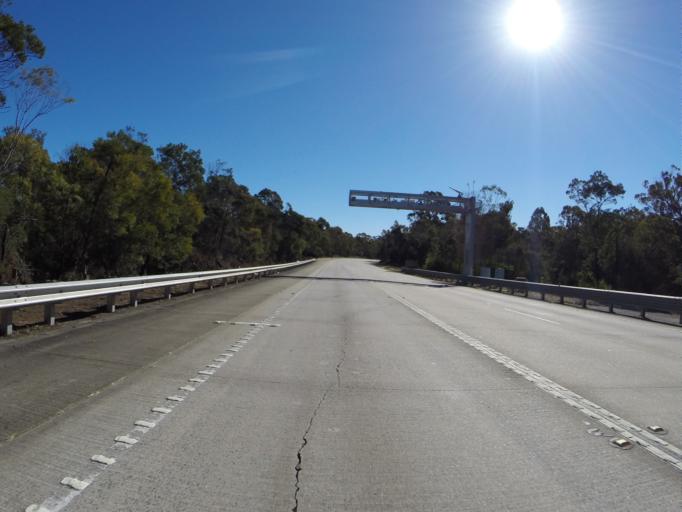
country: AU
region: New South Wales
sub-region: Wollondilly
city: Douglas Park
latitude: -34.2733
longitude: 150.7143
